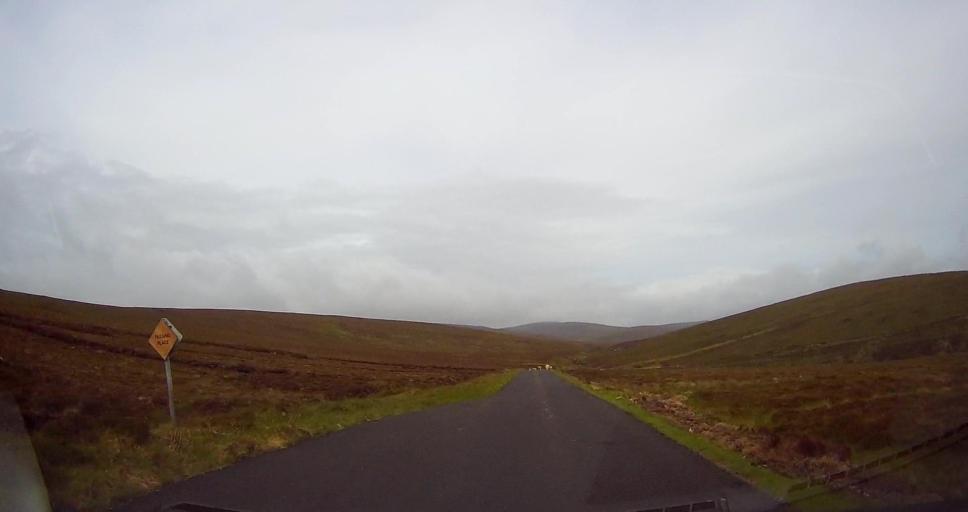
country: GB
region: Scotland
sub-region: Orkney Islands
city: Stromness
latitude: 58.8586
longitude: -3.2205
